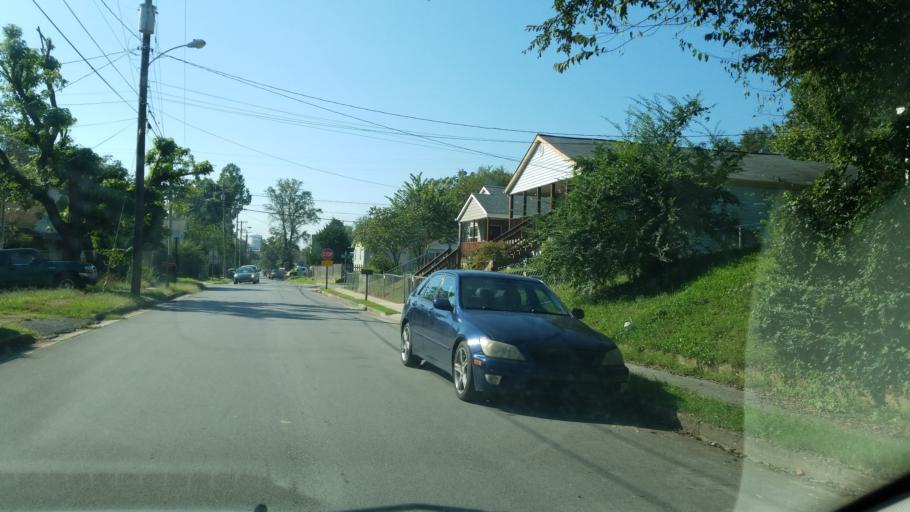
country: US
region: Tennessee
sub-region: Hamilton County
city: Chattanooga
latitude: 35.0725
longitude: -85.3097
